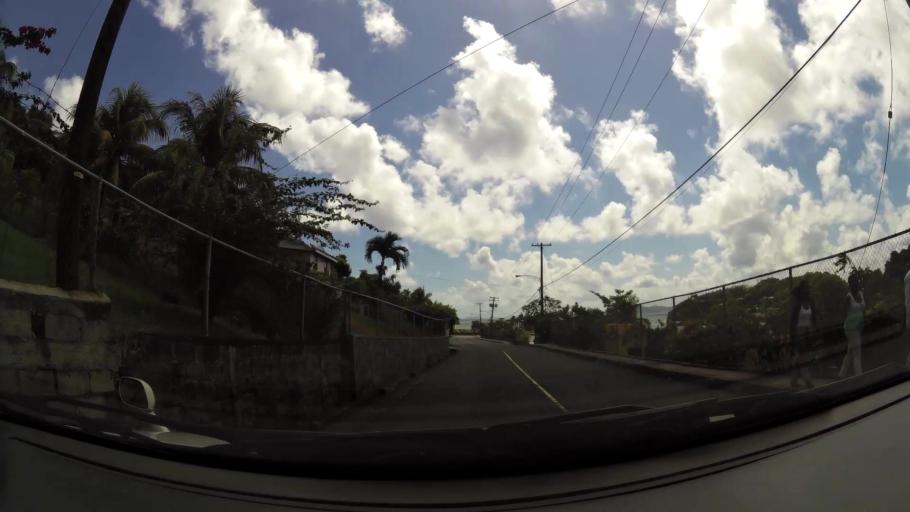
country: VC
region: Saint George
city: Kingstown
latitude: 13.1354
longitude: -61.2012
